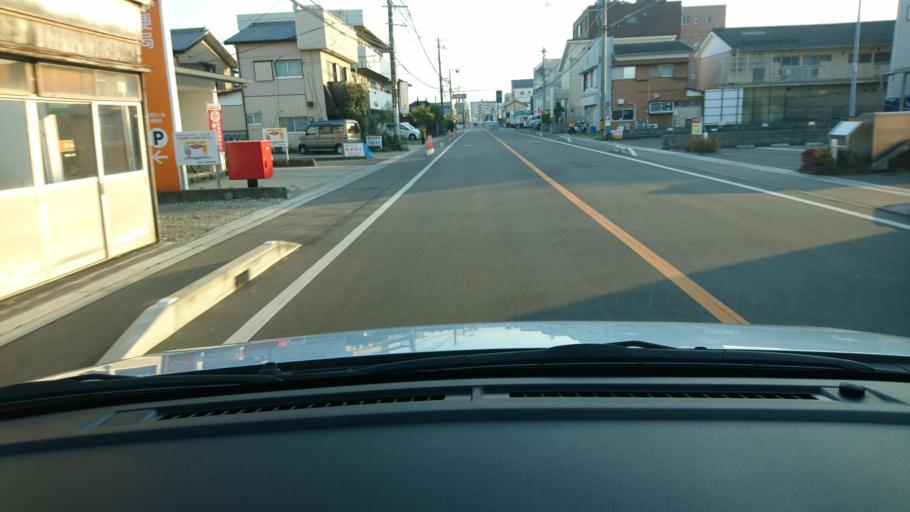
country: JP
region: Miyazaki
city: Miyazaki-shi
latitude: 31.9479
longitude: 131.4324
